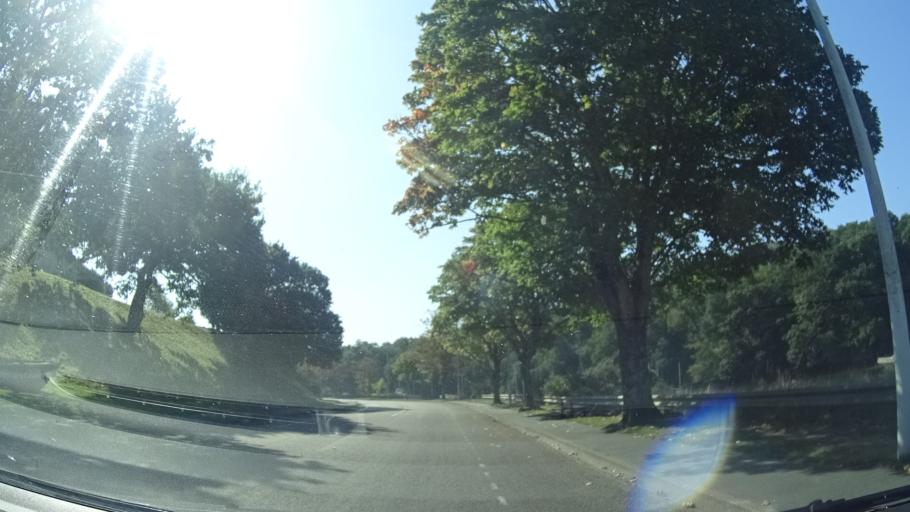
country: FR
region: Brittany
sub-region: Departement du Finistere
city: Douarnenez
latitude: 48.0861
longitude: -4.3320
